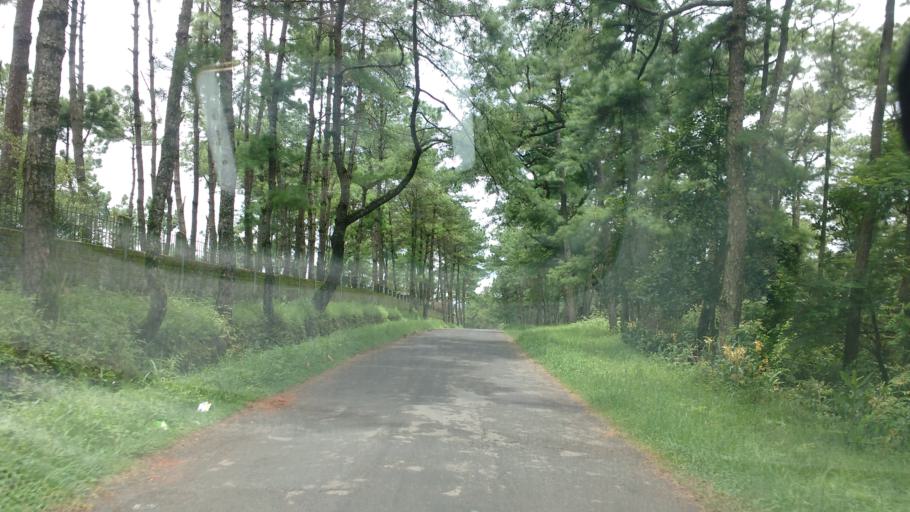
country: IN
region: Meghalaya
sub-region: East Khasi Hills
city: Shillong
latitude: 25.5427
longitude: 91.8238
